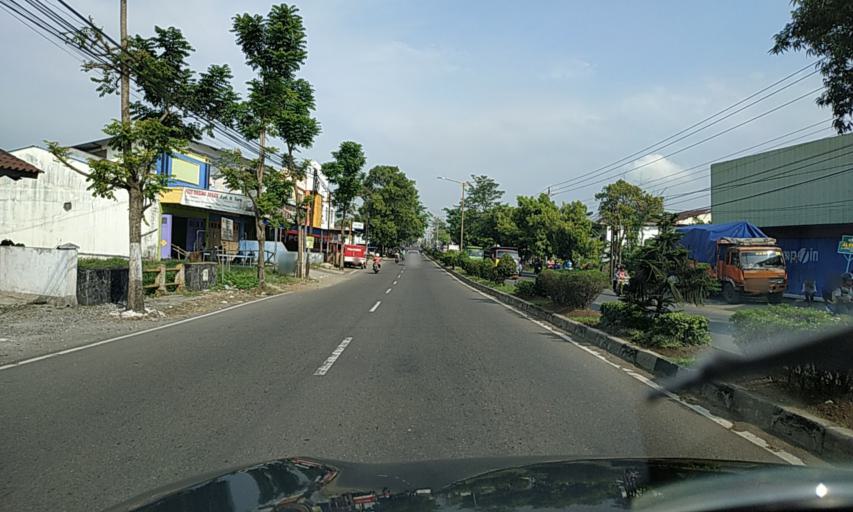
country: ID
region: Central Java
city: Purwokerto
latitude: -7.4218
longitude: 109.2089
